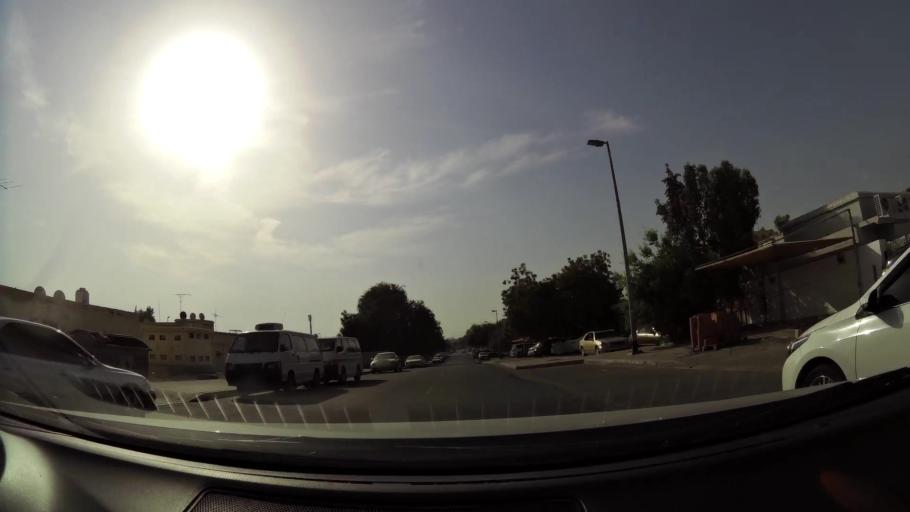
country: AE
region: Ash Shariqah
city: Sharjah
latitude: 25.2203
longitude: 55.3837
